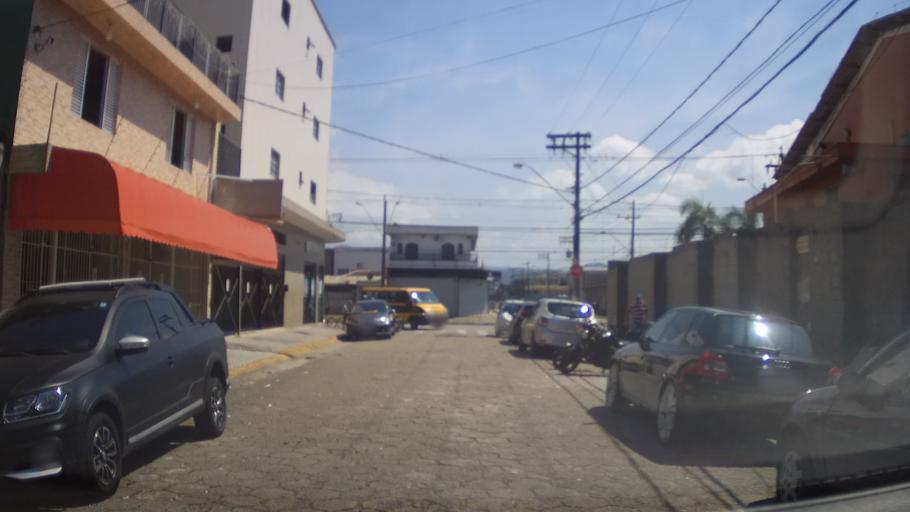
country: BR
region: Sao Paulo
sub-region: Praia Grande
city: Praia Grande
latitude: -24.0150
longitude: -46.4488
